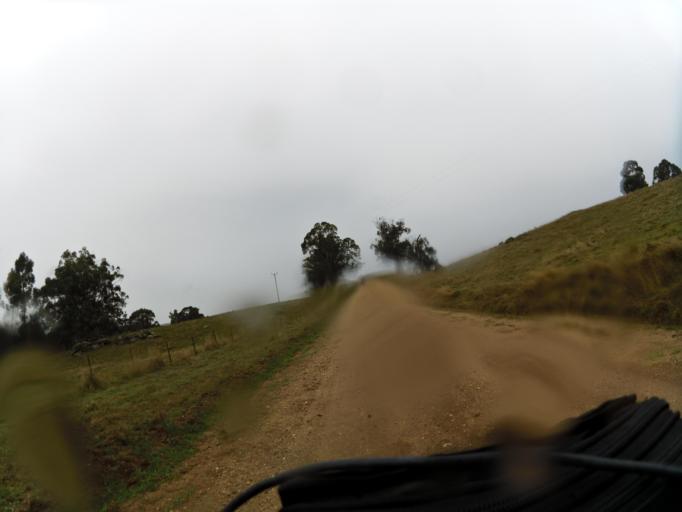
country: AU
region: New South Wales
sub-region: Greater Hume Shire
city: Holbrook
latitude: -36.1607
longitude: 147.4886
